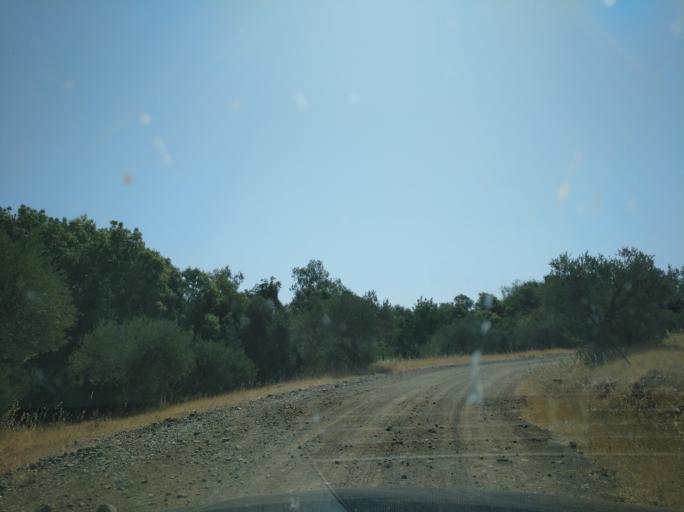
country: PT
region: Portalegre
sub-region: Campo Maior
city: Campo Maior
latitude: 39.0659
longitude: -7.0129
